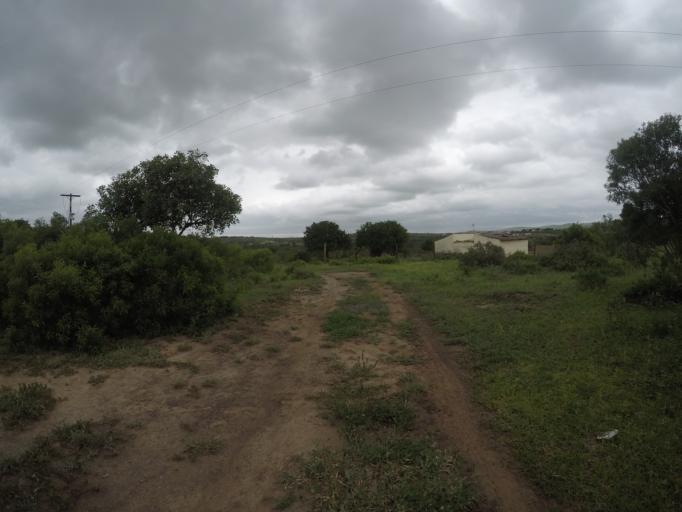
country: ZA
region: KwaZulu-Natal
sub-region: uThungulu District Municipality
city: Empangeni
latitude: -28.5931
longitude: 31.8462
